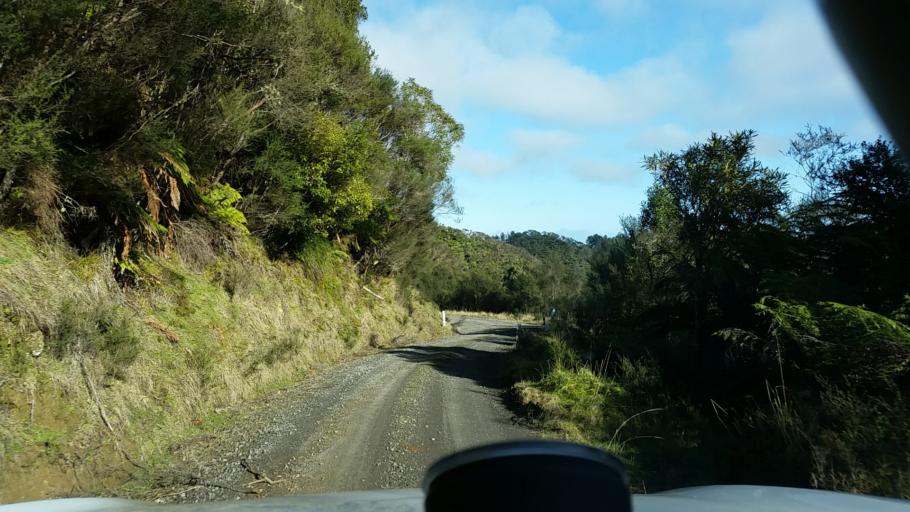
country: NZ
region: Taranaki
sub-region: South Taranaki District
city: Eltham
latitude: -39.4050
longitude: 174.5595
